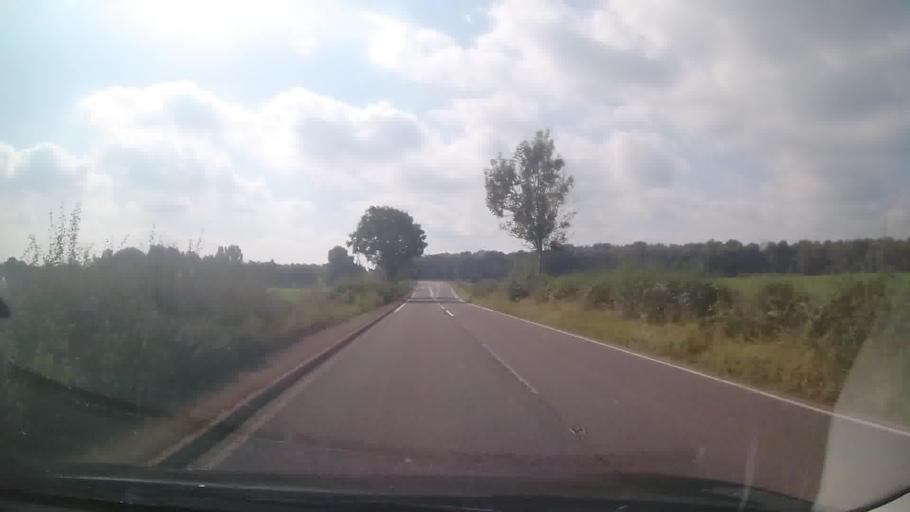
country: GB
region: England
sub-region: Cheshire West and Chester
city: Bickley
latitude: 53.0436
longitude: -2.6740
